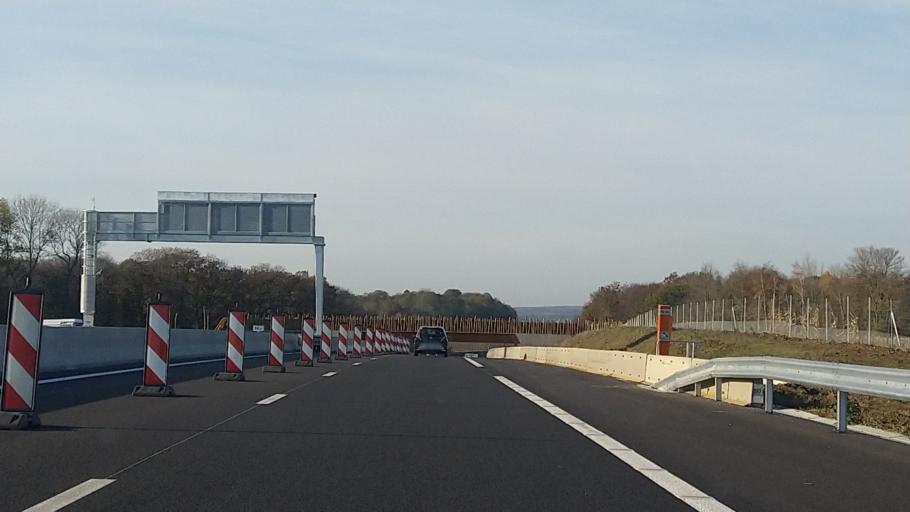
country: FR
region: Ile-de-France
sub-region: Departement du Val-d'Oise
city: Maffliers
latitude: 49.0889
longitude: 2.3113
